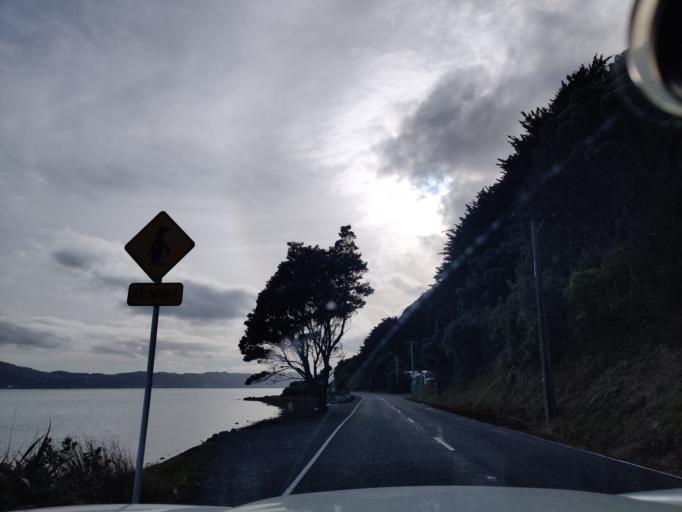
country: NZ
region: Wellington
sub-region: Wellington City
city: Wellington
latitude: -41.3091
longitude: 174.8134
